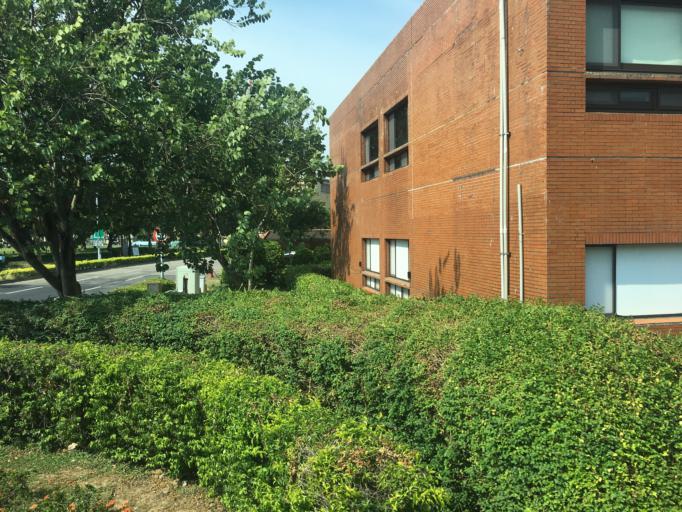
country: TW
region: Taiwan
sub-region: Hsinchu
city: Hsinchu
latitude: 24.7753
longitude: 121.0047
